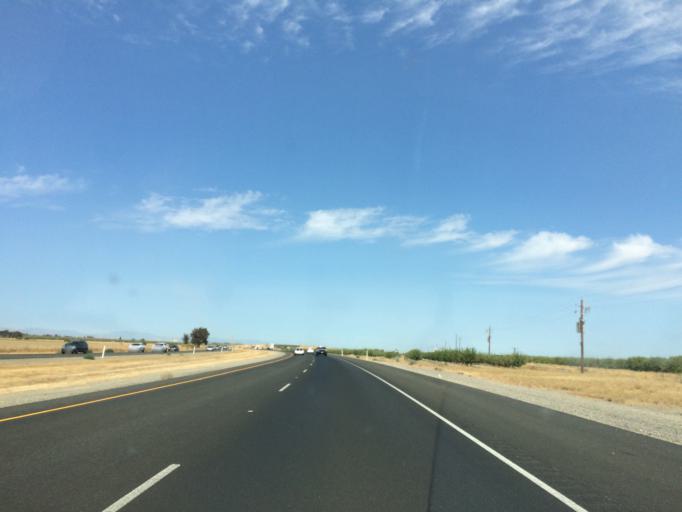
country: US
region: California
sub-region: Yolo County
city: Dunnigan
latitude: 38.9480
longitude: -122.0116
